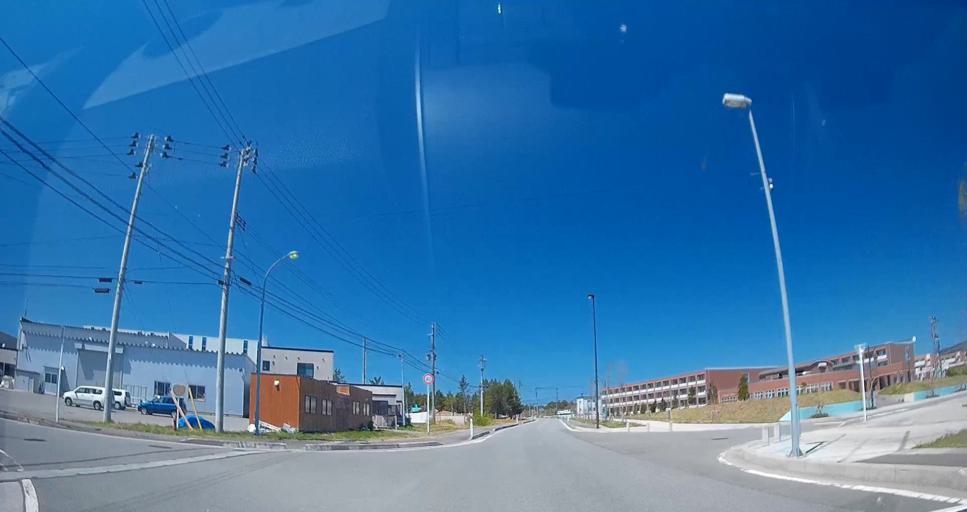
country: JP
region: Aomori
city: Misawa
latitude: 40.9692
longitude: 141.3621
